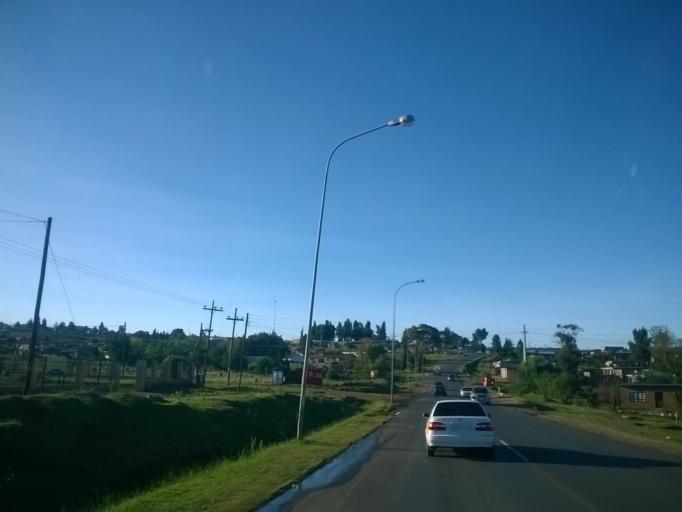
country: LS
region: Maseru
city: Maseru
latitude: -29.2801
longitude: 27.5285
